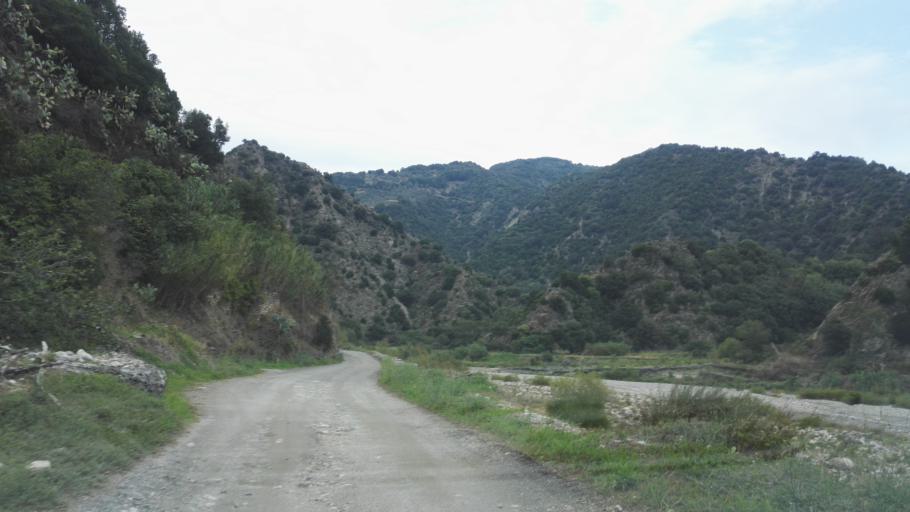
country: IT
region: Calabria
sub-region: Provincia di Reggio Calabria
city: Caulonia
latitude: 38.4195
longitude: 16.3762
